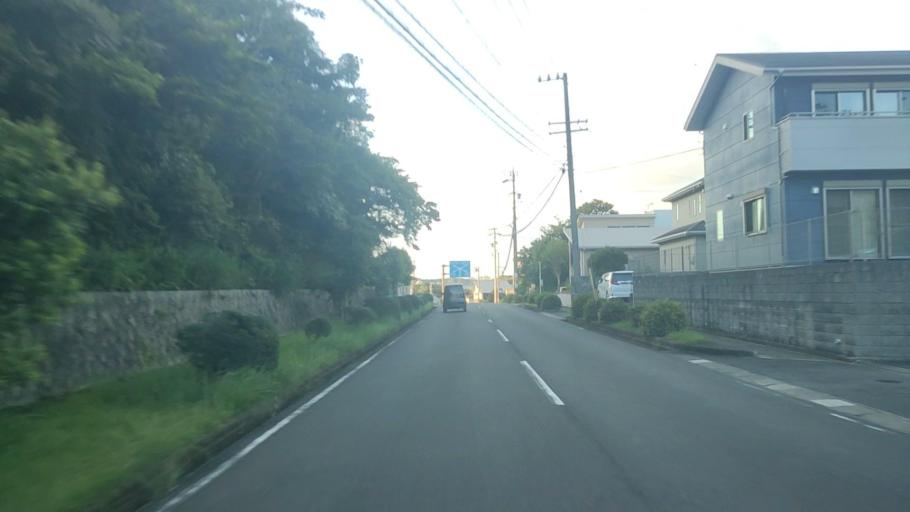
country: JP
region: Mie
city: Toba
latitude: 34.3243
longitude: 136.8220
